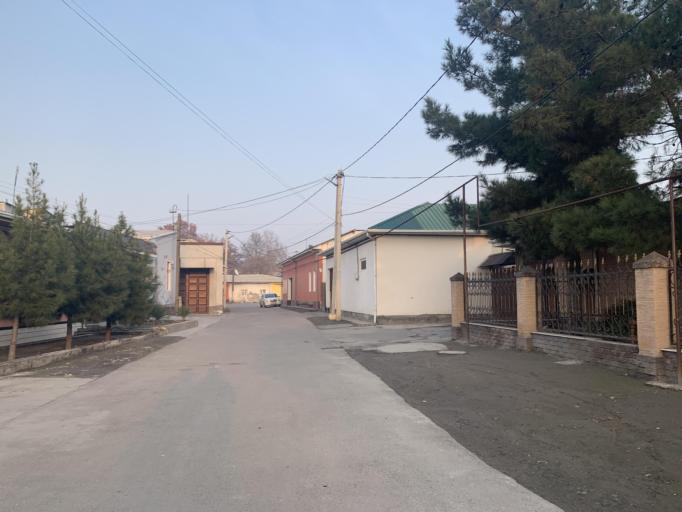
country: UZ
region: Fergana
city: Qo`qon
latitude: 40.5352
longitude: 70.9324
